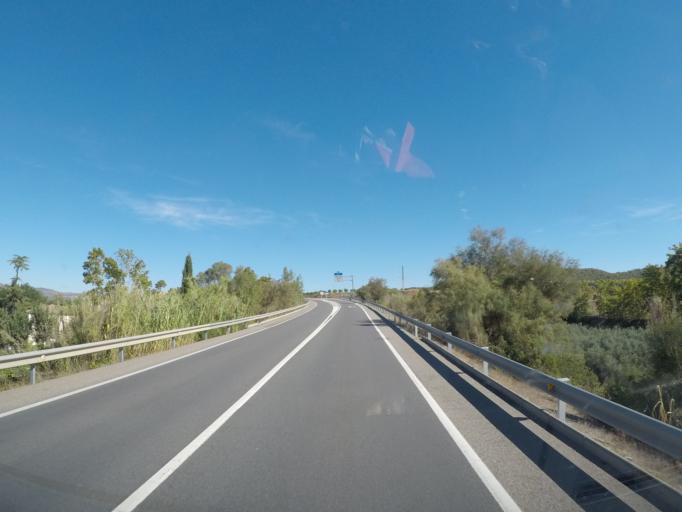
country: ES
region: Catalonia
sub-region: Provincia de Tarragona
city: Ginestar
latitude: 41.0689
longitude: 0.6633
